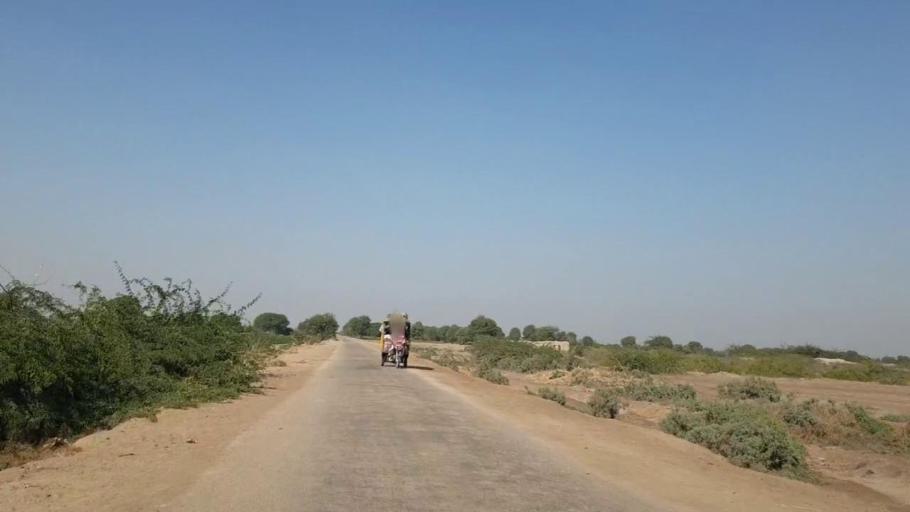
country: PK
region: Sindh
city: Digri
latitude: 25.0046
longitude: 69.1064
